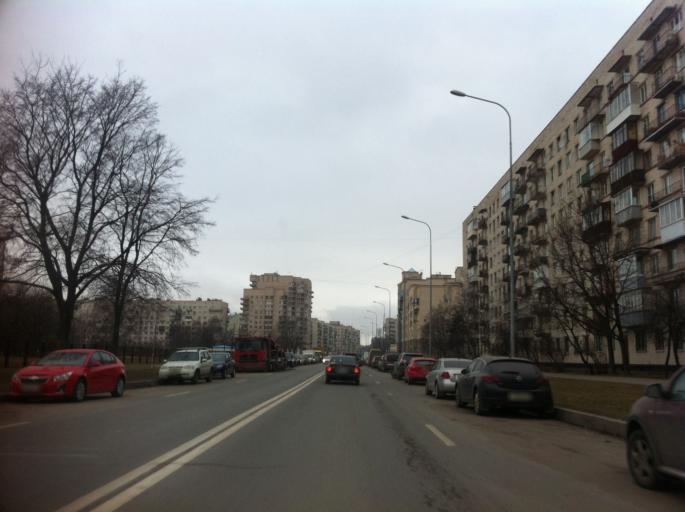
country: RU
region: St.-Petersburg
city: Dachnoye
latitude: 59.8380
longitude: 30.2420
